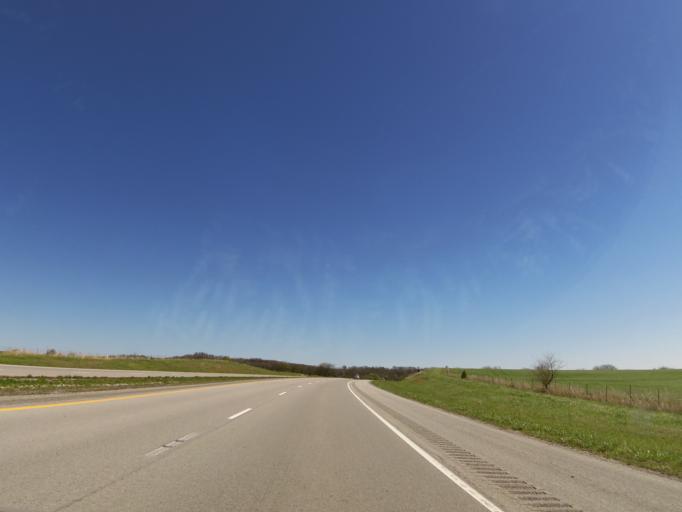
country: US
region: Kentucky
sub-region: Logan County
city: Auburn
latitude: 36.8899
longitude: -86.6542
